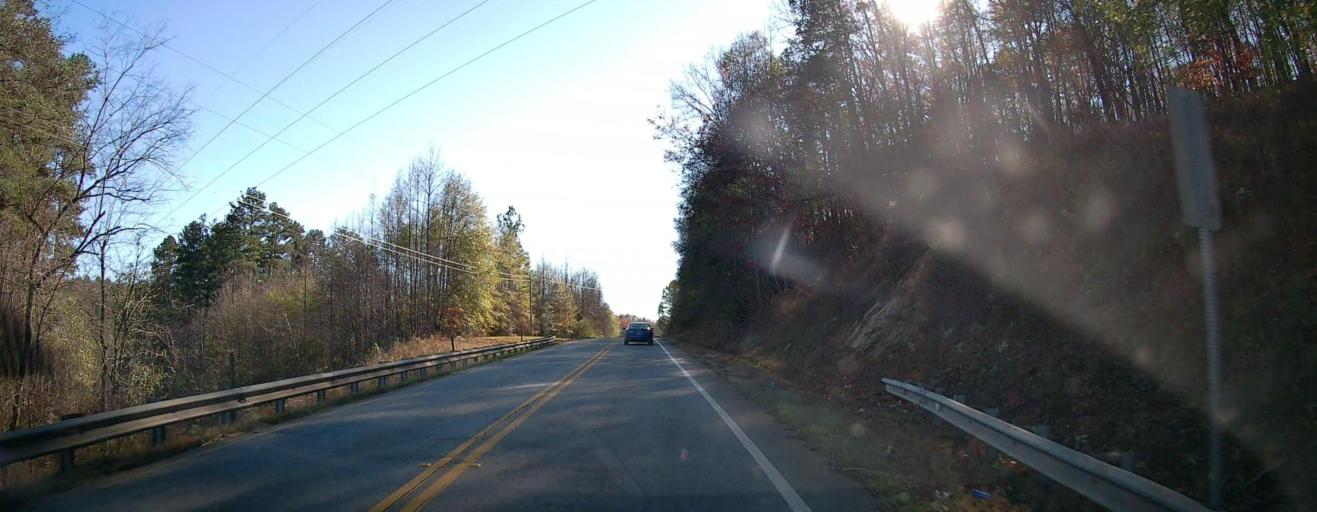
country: US
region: Georgia
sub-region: Hall County
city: Lula
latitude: 34.4132
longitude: -83.7090
